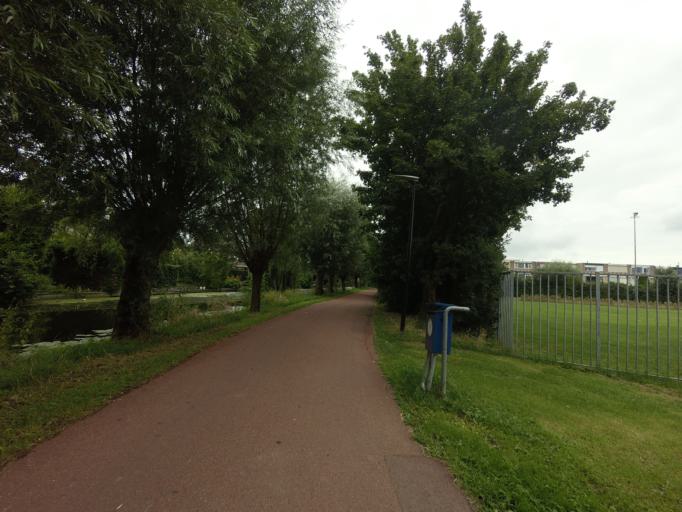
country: NL
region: South Holland
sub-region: Gemeente Alblasserdam
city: Alblasserdam
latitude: 51.8720
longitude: 4.6506
